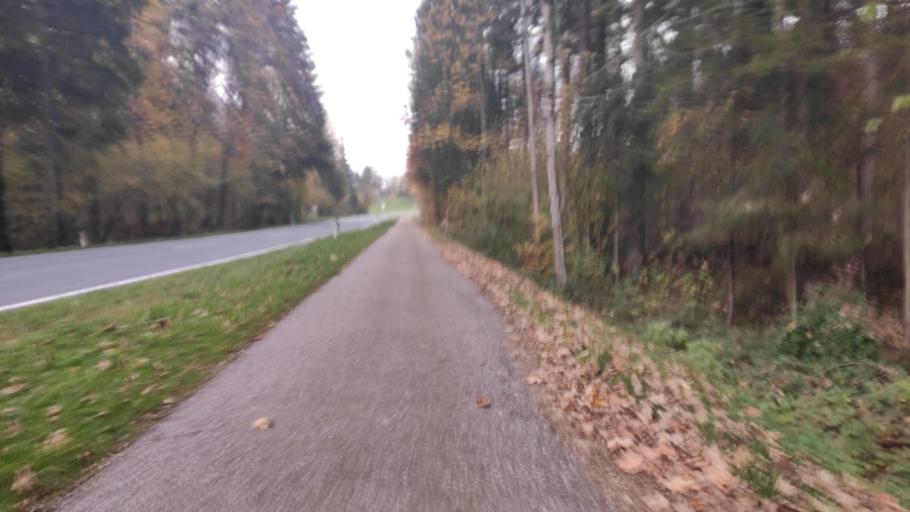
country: AT
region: Salzburg
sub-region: Politischer Bezirk Salzburg-Umgebung
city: Ebenau
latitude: 47.7730
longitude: 13.1817
